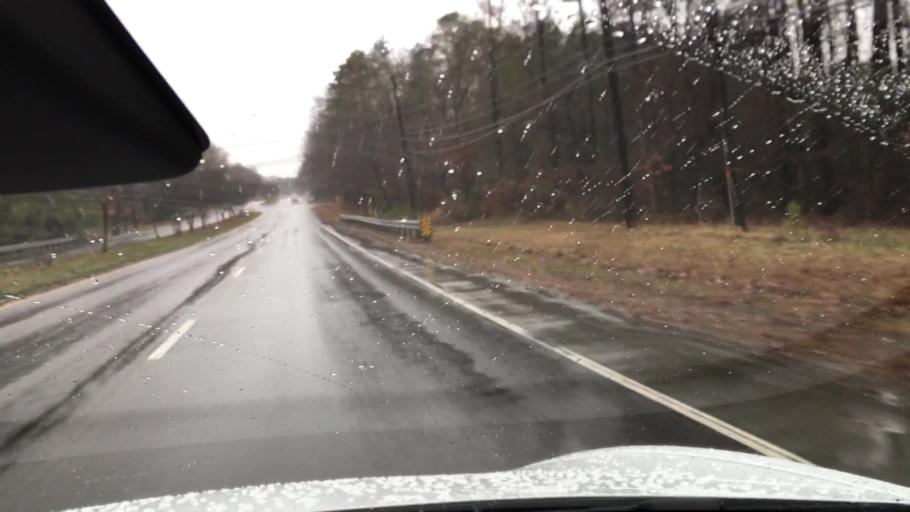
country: US
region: Virginia
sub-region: Chesterfield County
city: Bon Air
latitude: 37.5347
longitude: -77.5683
